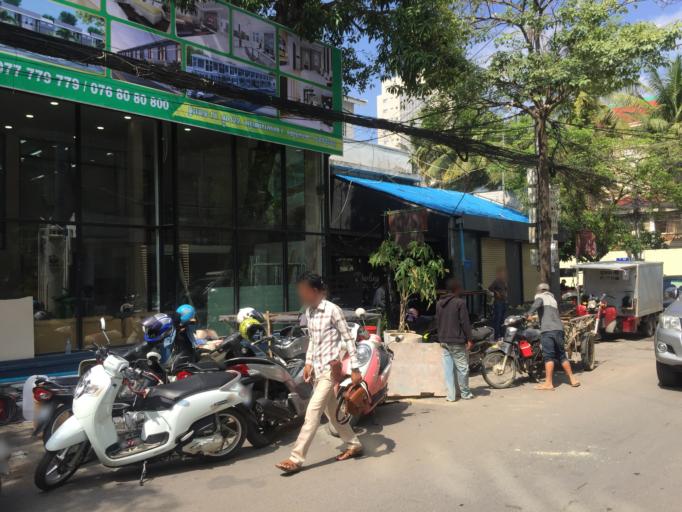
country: KH
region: Phnom Penh
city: Phnom Penh
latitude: 11.5511
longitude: 104.9272
